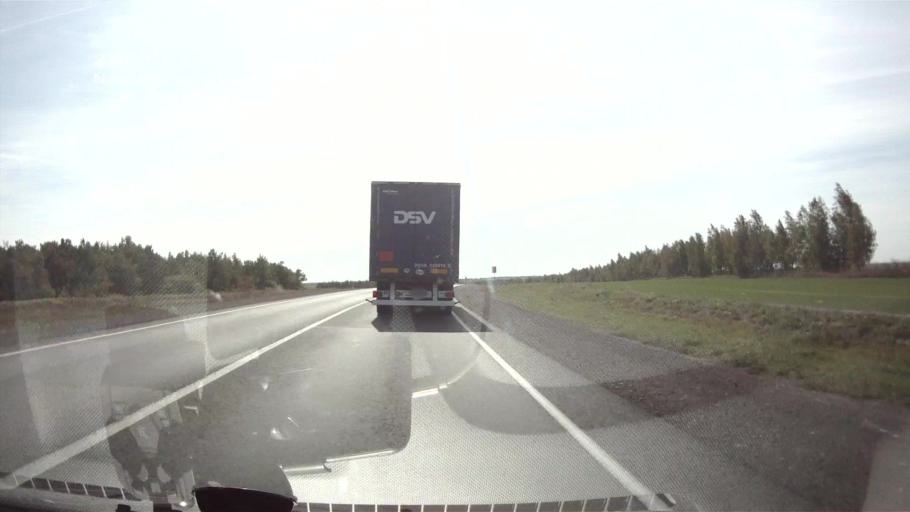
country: RU
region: Samara
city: Syzran'
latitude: 52.9325
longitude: 48.3074
